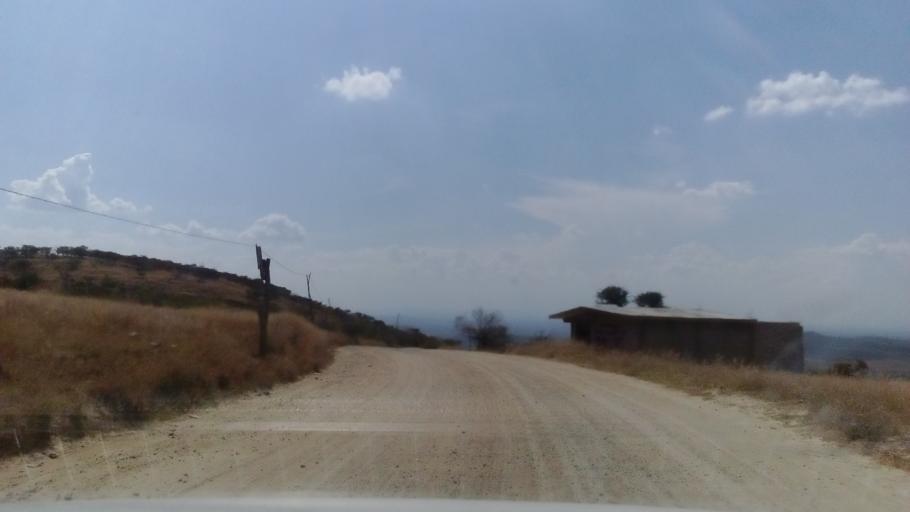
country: MX
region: Guanajuato
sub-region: Silao de la Victoria
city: Loma de Yerbabuena
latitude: 21.0821
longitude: -101.4480
